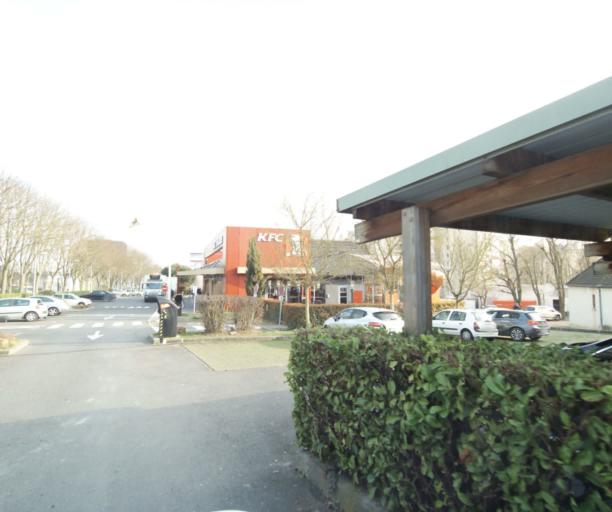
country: FR
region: Ile-de-France
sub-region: Departement du Val-d'Oise
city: Cergy-Pontoise
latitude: 49.0453
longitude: 2.0688
